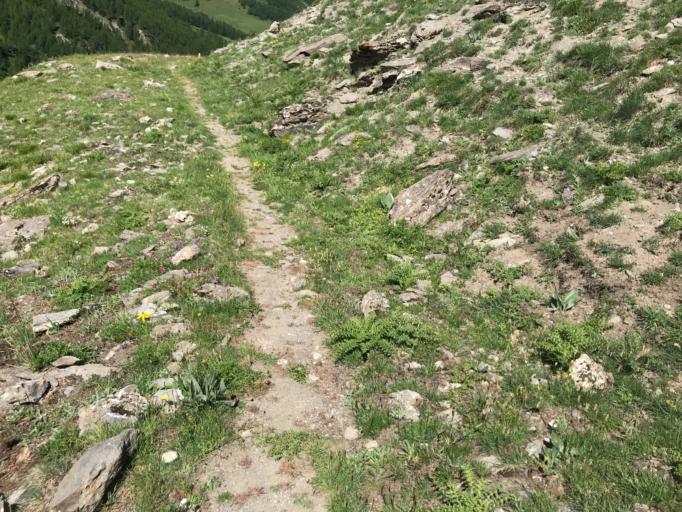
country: IT
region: Piedmont
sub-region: Provincia di Cuneo
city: Pontechianale
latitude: 44.7121
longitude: 6.9267
